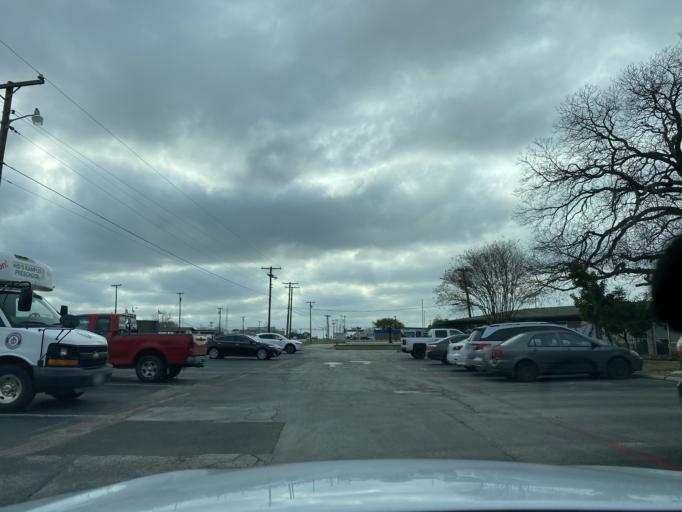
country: US
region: Texas
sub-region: Tarrant County
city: Euless
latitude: 32.8273
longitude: -97.1048
